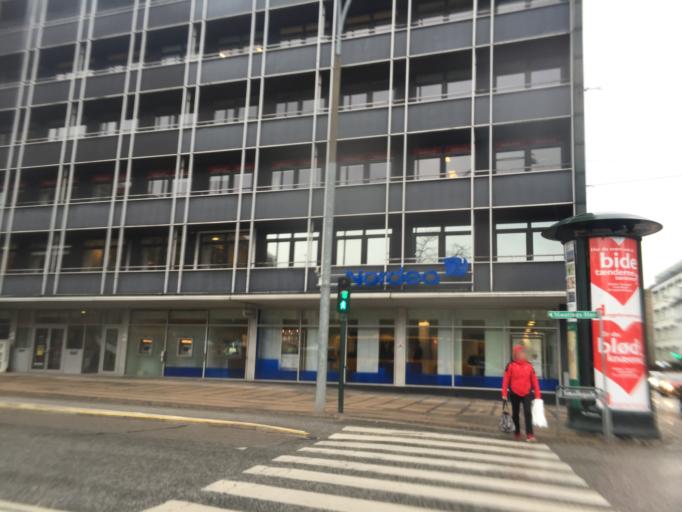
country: DK
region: Capital Region
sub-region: Frederiksberg Kommune
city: Frederiksberg
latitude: 55.6784
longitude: 12.5331
